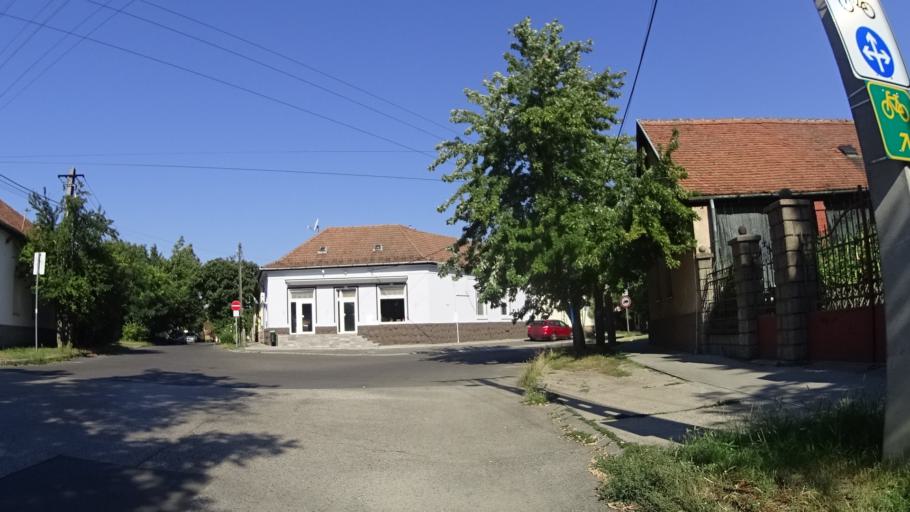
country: HU
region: Pest
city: Dunakeszi
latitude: 47.6302
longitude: 19.1344
